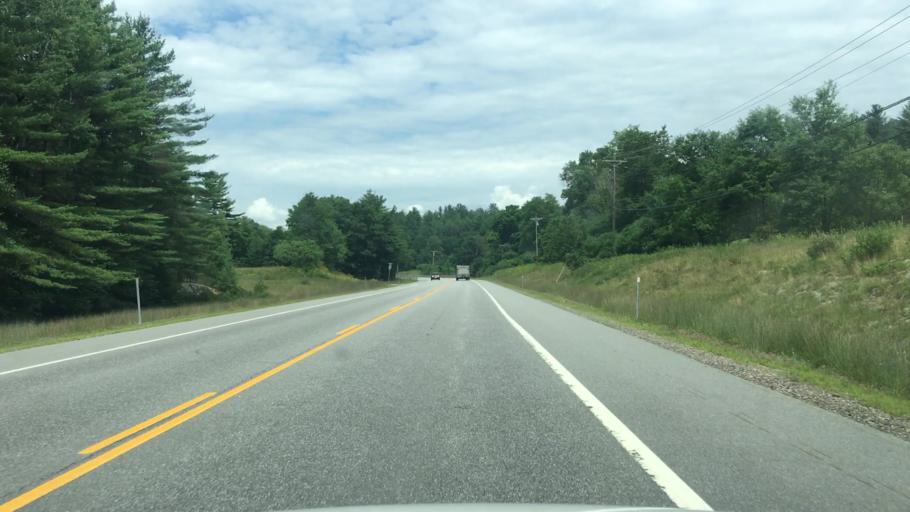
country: US
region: New Hampshire
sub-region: Grafton County
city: Rumney
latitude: 43.8530
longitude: -71.9109
